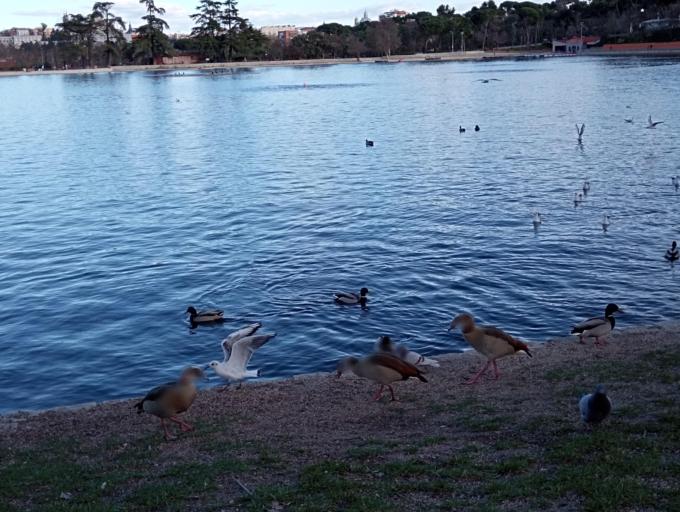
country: ES
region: Madrid
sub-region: Provincia de Madrid
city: Moncloa-Aravaca
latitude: 40.4193
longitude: -3.7345
